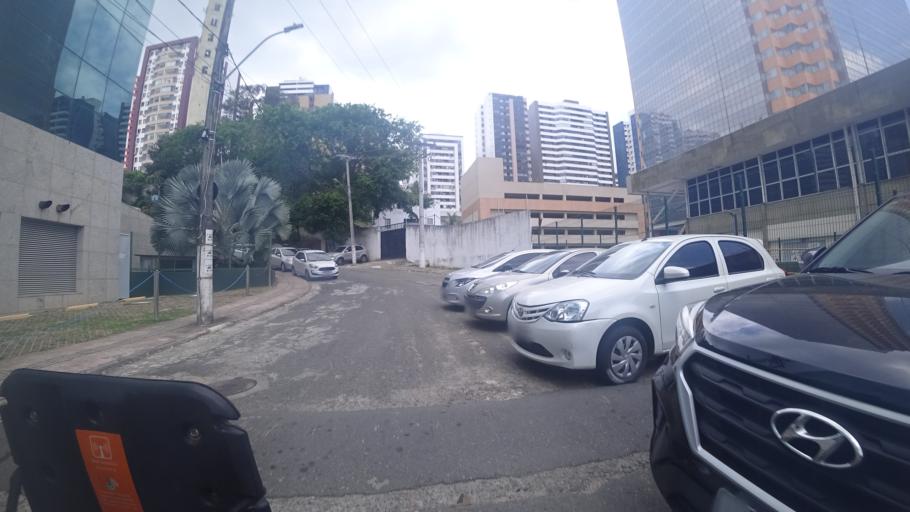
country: BR
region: Bahia
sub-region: Salvador
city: Salvador
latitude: -12.9971
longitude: -38.4668
